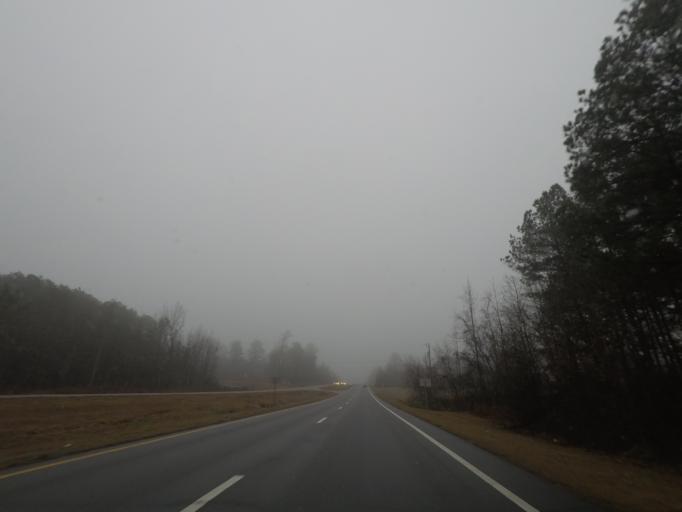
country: US
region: North Carolina
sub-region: Lee County
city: Sanford
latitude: 35.3997
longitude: -79.2315
